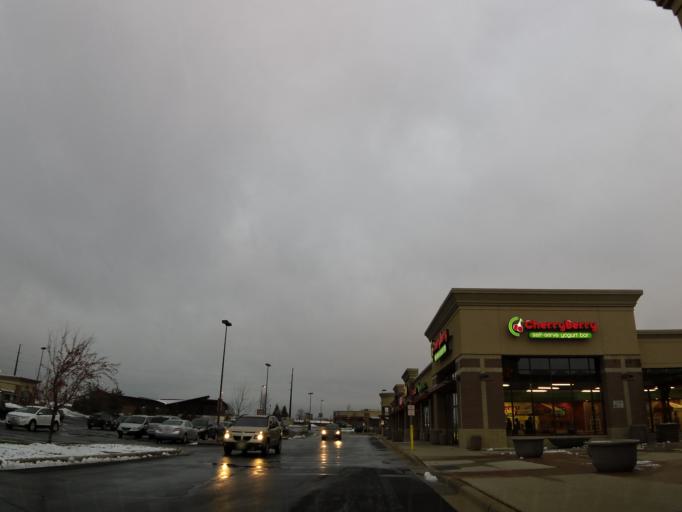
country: US
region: Minnesota
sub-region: Dakota County
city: Apple Valley
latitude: 44.6934
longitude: -93.2153
